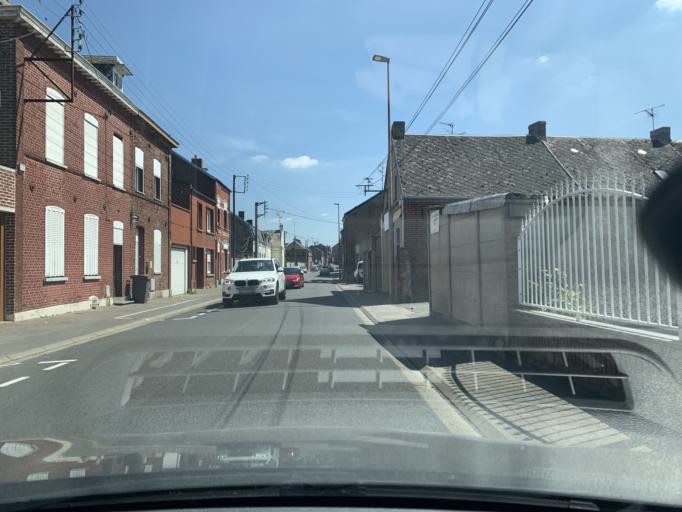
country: FR
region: Nord-Pas-de-Calais
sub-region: Departement du Nord
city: Caudry
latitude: 50.1228
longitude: 3.4013
